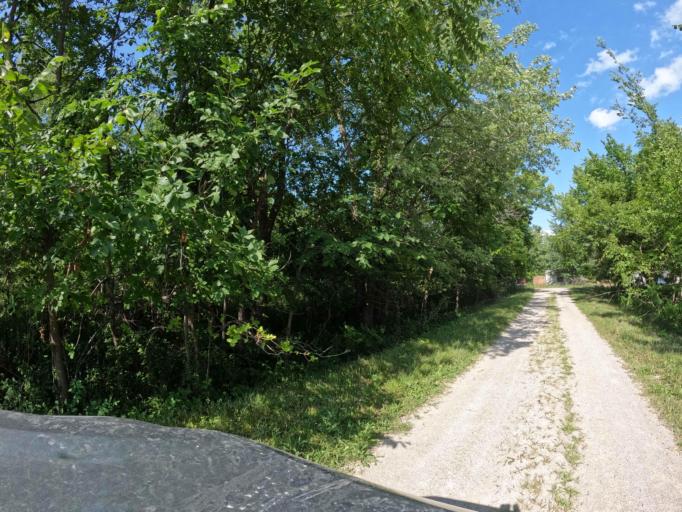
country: US
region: Iowa
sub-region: Appanoose County
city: Centerville
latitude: 40.7202
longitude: -93.0259
